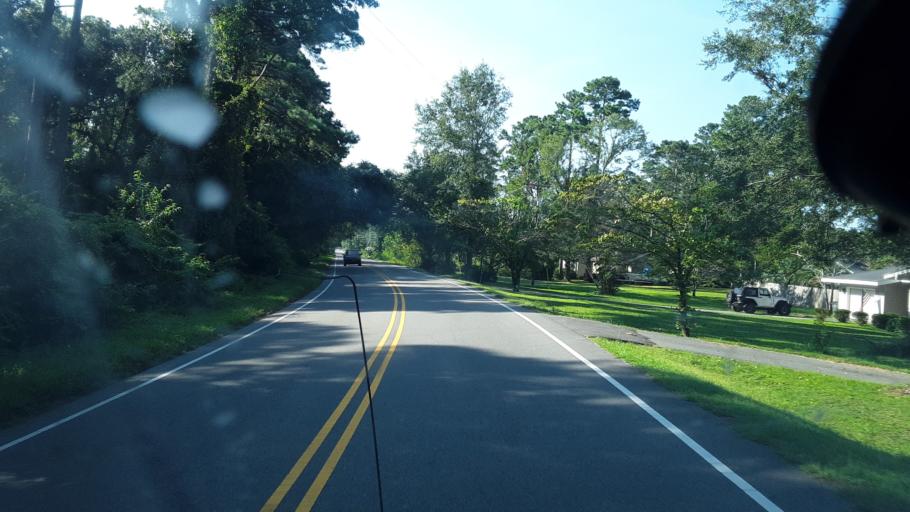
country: US
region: North Carolina
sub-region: Brunswick County
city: Belville
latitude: 34.2130
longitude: -77.9839
